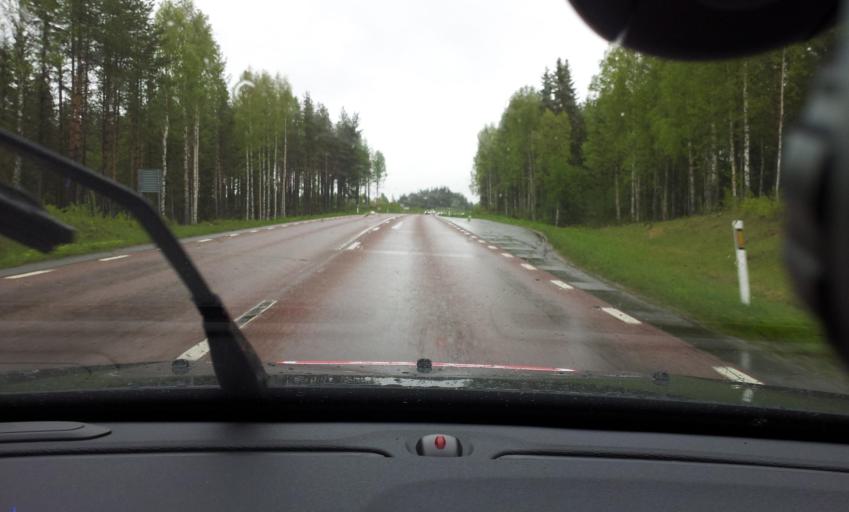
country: SE
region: Jaemtland
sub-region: Bergs Kommun
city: Hoverberg
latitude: 62.7895
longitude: 14.4686
